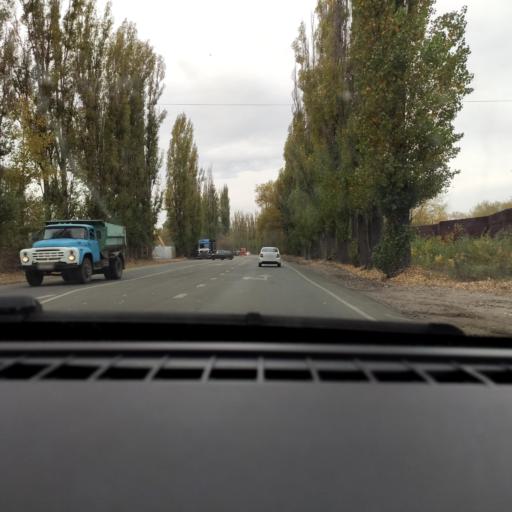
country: RU
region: Voronezj
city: Maslovka
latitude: 51.6231
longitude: 39.2443
